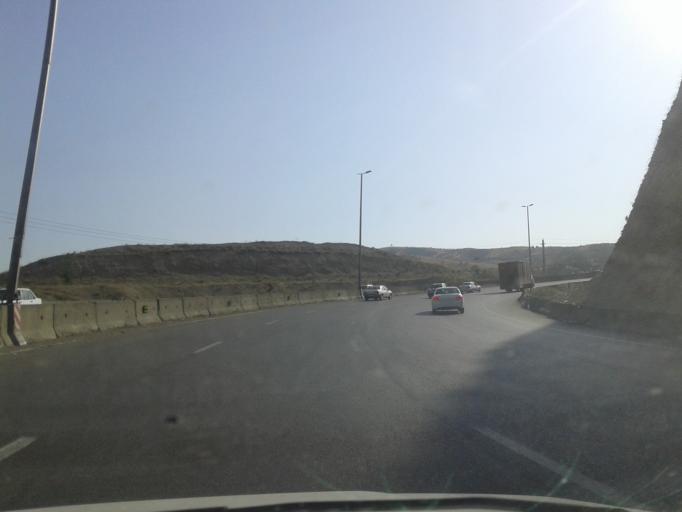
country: IR
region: Tehran
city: Pakdasht
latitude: 35.7360
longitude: 51.6774
